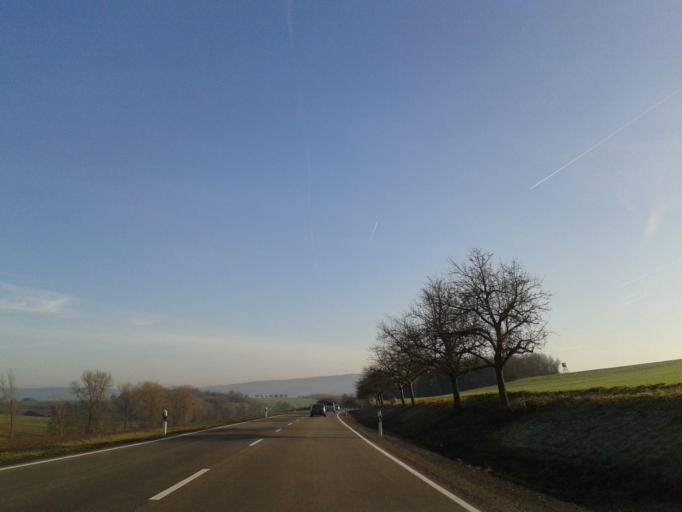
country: DE
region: Bavaria
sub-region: Regierungsbezirk Unterfranken
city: Hofheim in Unterfranken
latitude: 50.1246
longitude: 10.4948
